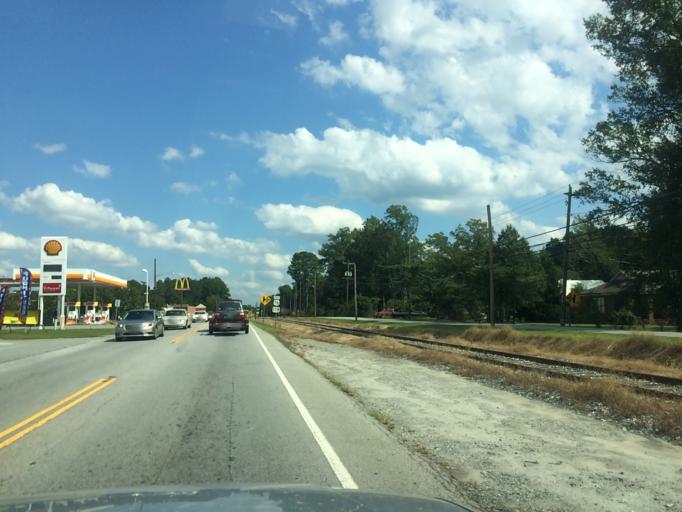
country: US
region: South Carolina
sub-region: Anderson County
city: Belton
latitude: 34.5165
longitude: -82.4873
